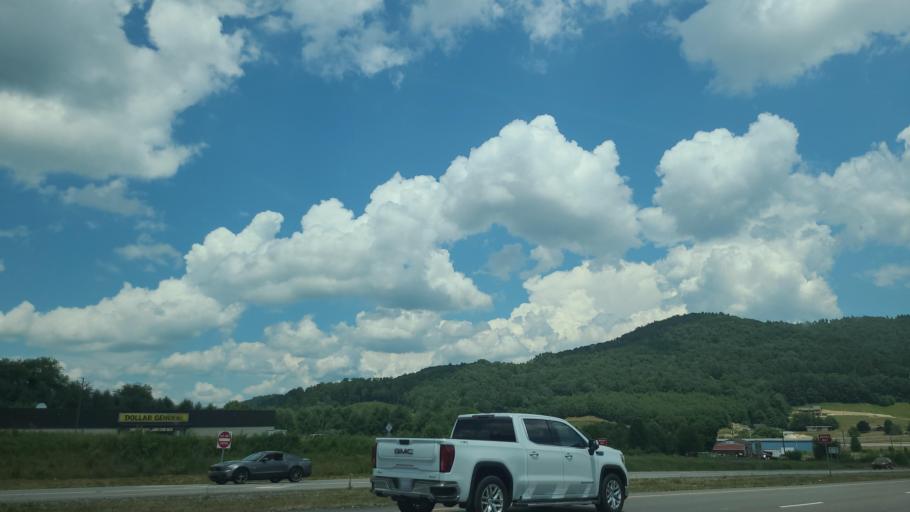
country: US
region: North Carolina
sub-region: Watauga County
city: Boone
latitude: 36.2384
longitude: -81.5158
